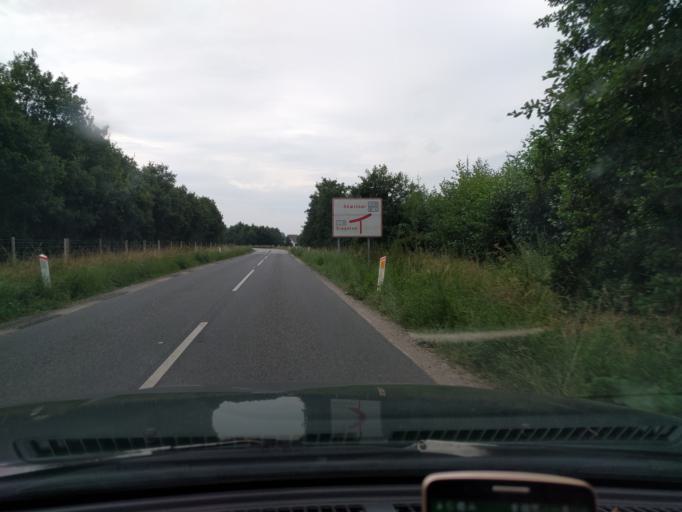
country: DK
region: Zealand
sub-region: Slagelse Kommune
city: Skaelskor
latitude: 55.2779
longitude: 11.2748
